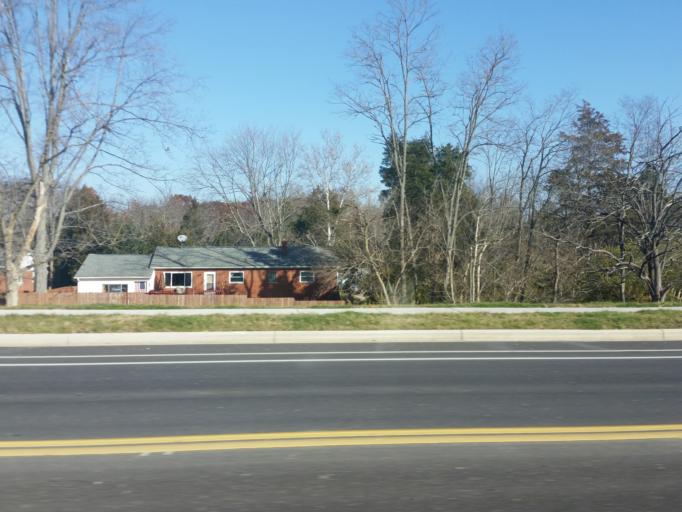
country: US
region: Ohio
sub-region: Butler County
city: Oxford
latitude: 39.4919
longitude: -84.7237
